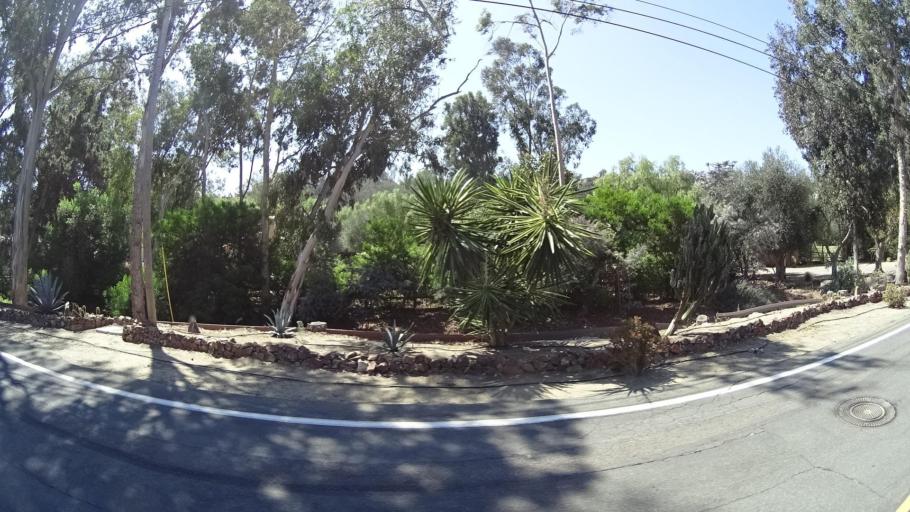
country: US
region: California
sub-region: San Diego County
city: Rancho Santa Fe
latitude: 33.0085
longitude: -117.2261
